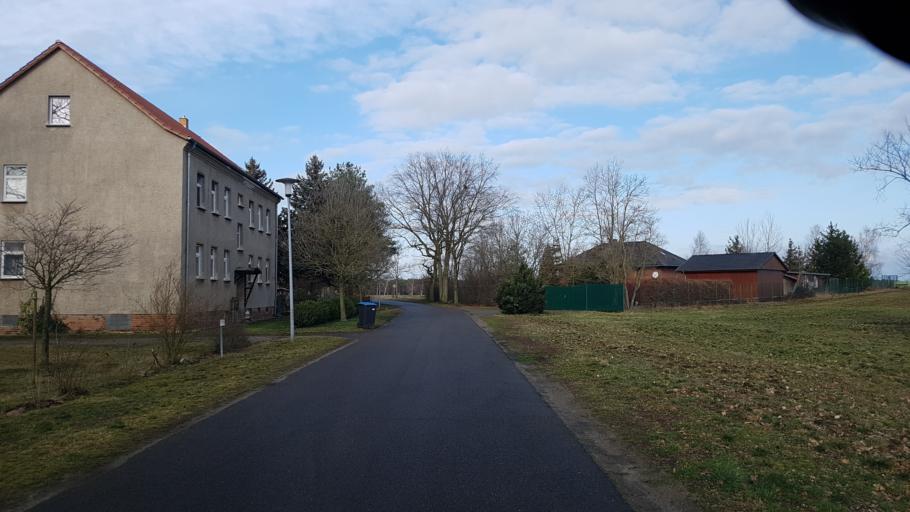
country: DE
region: Brandenburg
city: Schlieben
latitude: 51.6974
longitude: 13.3278
